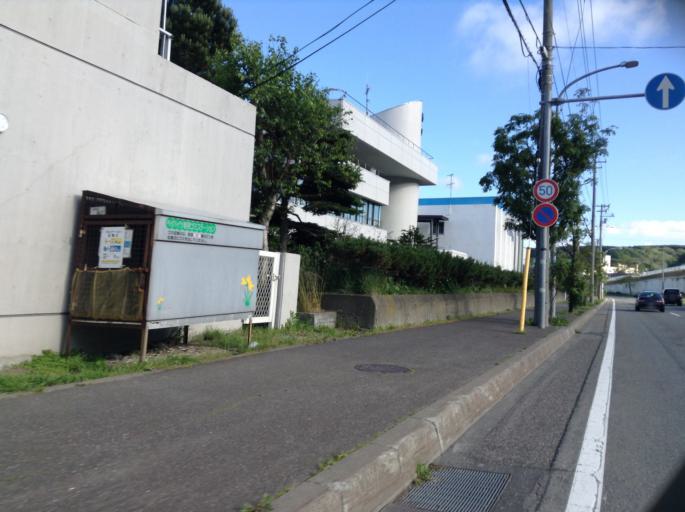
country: JP
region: Hokkaido
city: Wakkanai
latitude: 45.4068
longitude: 141.6758
